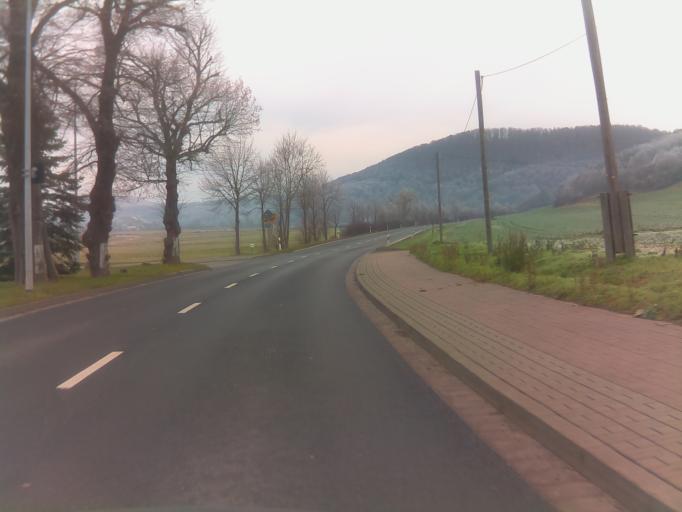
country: DE
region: Thuringia
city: Dorndorf
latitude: 50.8428
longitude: 10.1132
